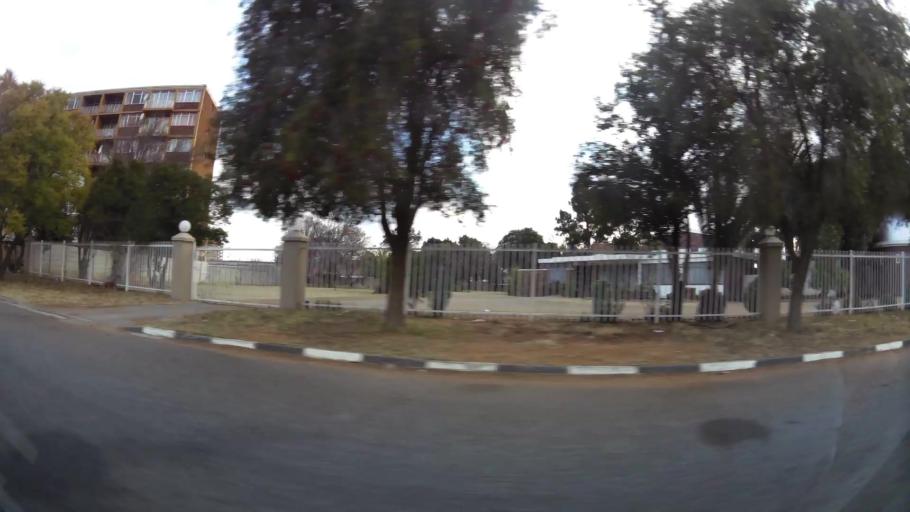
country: ZA
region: Orange Free State
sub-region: Lejweleputswa District Municipality
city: Welkom
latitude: -27.9812
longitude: 26.7300
